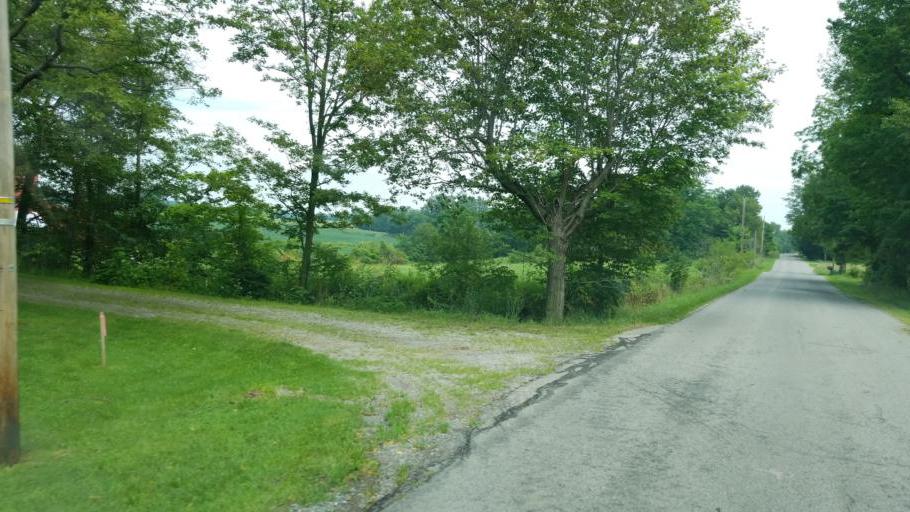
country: US
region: Ohio
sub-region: Logan County
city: Northwood
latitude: 40.4197
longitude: -83.7350
